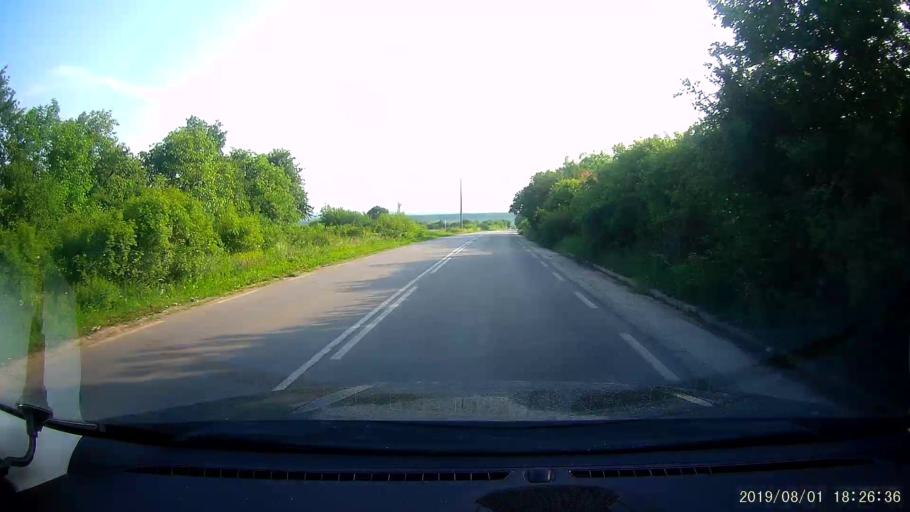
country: BG
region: Shumen
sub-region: Obshtina Venets
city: Venets
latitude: 43.5983
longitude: 26.9894
